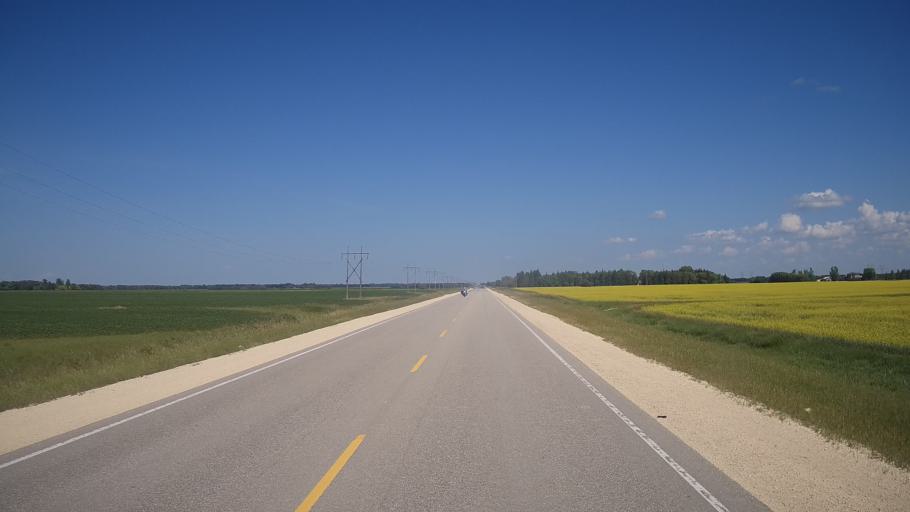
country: CA
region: Manitoba
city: Stonewall
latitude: 50.1227
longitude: -97.3997
